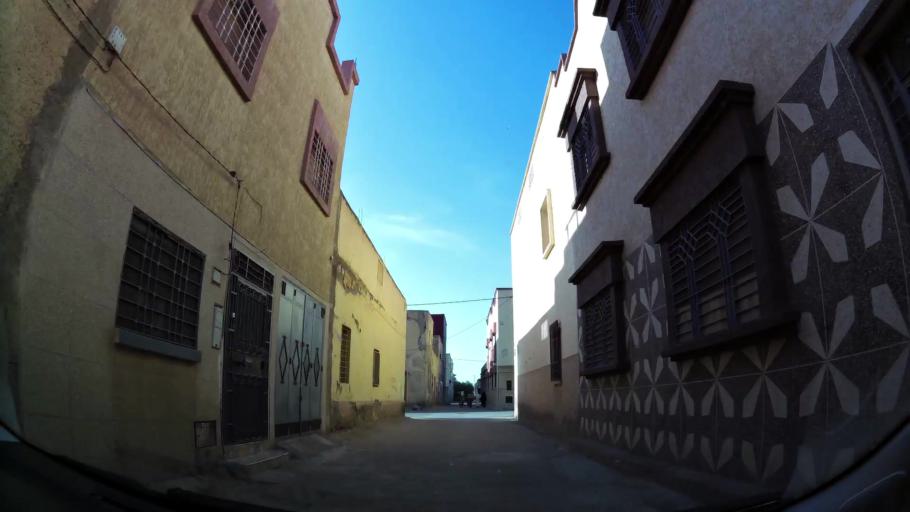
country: MA
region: Oriental
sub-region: Oujda-Angad
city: Oujda
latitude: 34.6954
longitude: -1.9180
